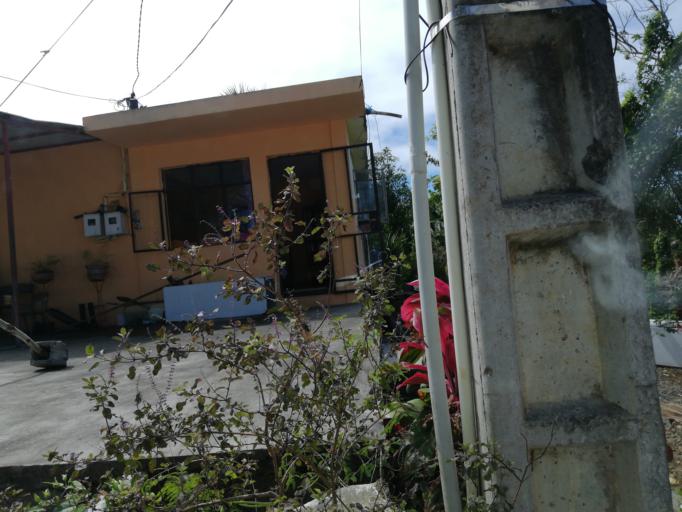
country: MU
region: Grand Port
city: Plaine Magnien
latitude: -20.4650
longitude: 57.6755
